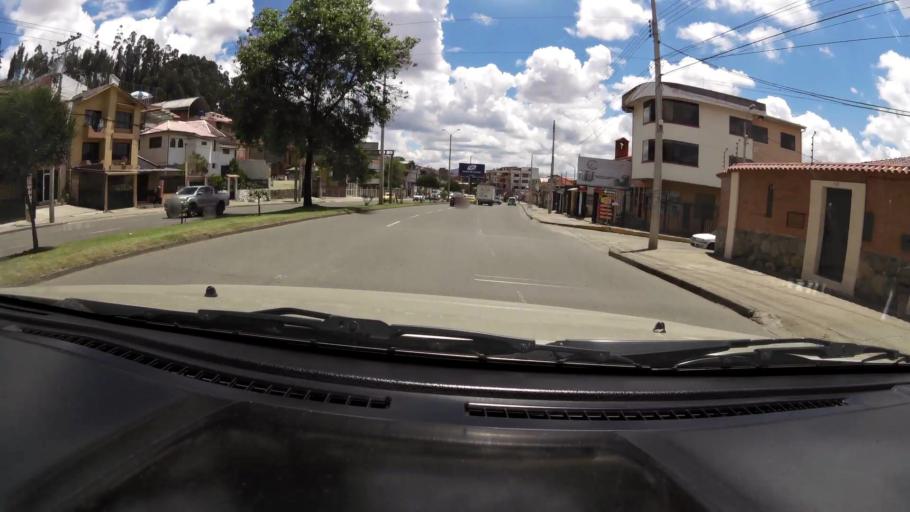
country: EC
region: Azuay
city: Cuenca
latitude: -2.8888
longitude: -79.0205
